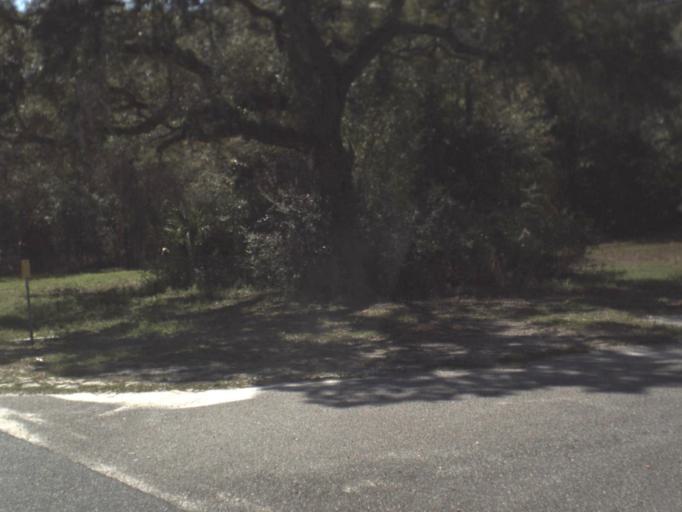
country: US
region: Florida
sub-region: Wakulla County
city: Crawfordville
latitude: 30.0252
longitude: -84.3903
